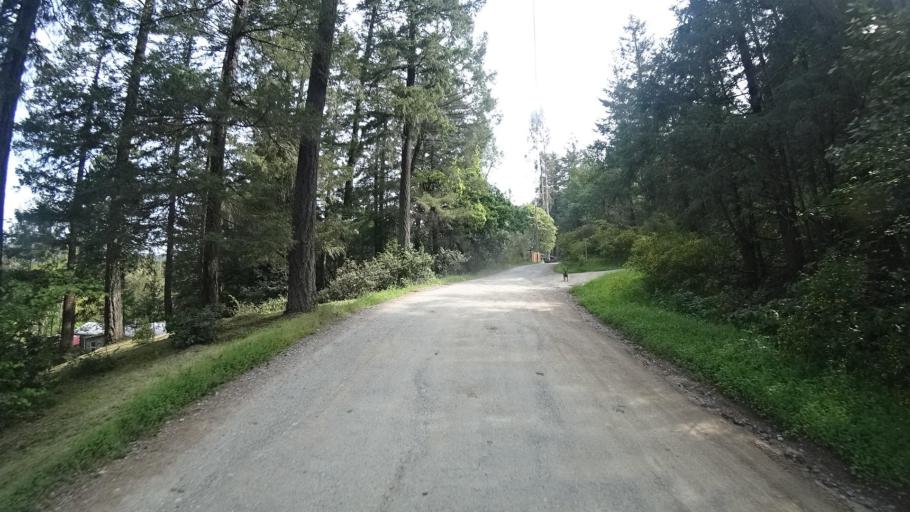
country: US
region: California
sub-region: Humboldt County
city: Redway
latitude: 40.2365
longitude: -123.8183
